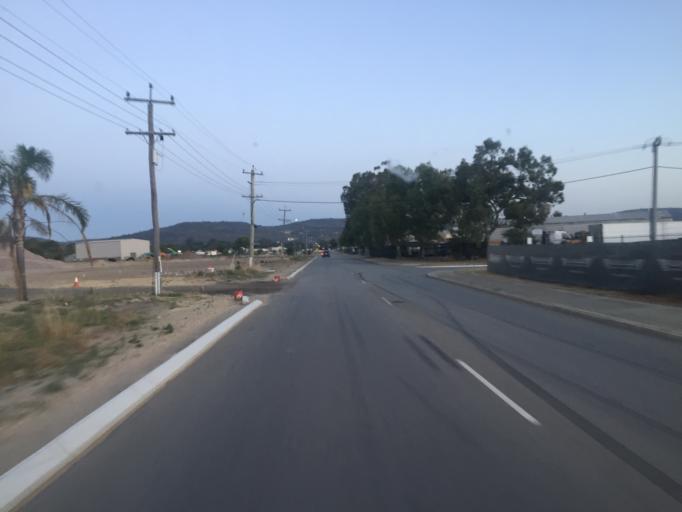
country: AU
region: Western Australia
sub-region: Gosnells
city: Maddington
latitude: -32.0329
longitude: 115.9978
